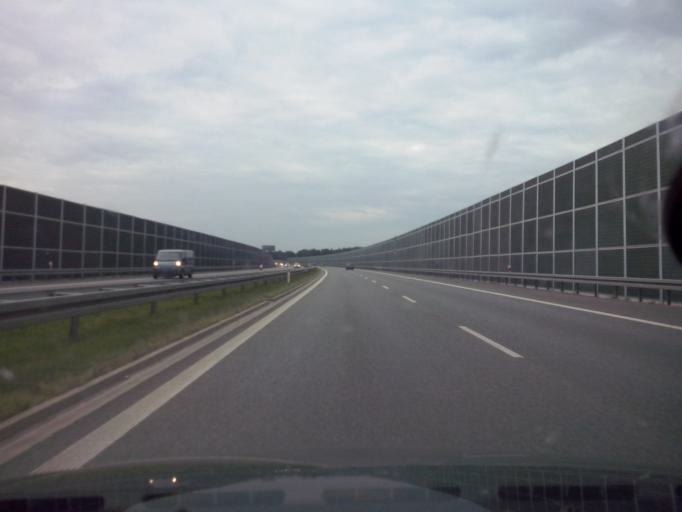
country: PL
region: Lesser Poland Voivodeship
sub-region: Powiat bochenski
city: Bochnia
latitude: 50.0049
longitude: 20.4159
